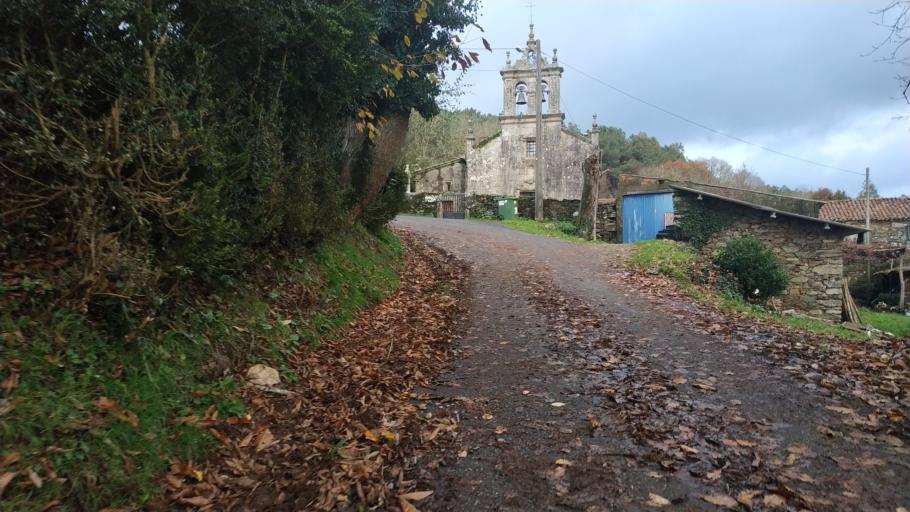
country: ES
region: Galicia
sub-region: Provincia de Pontevedra
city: Silleda
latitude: 42.7831
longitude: -8.1700
